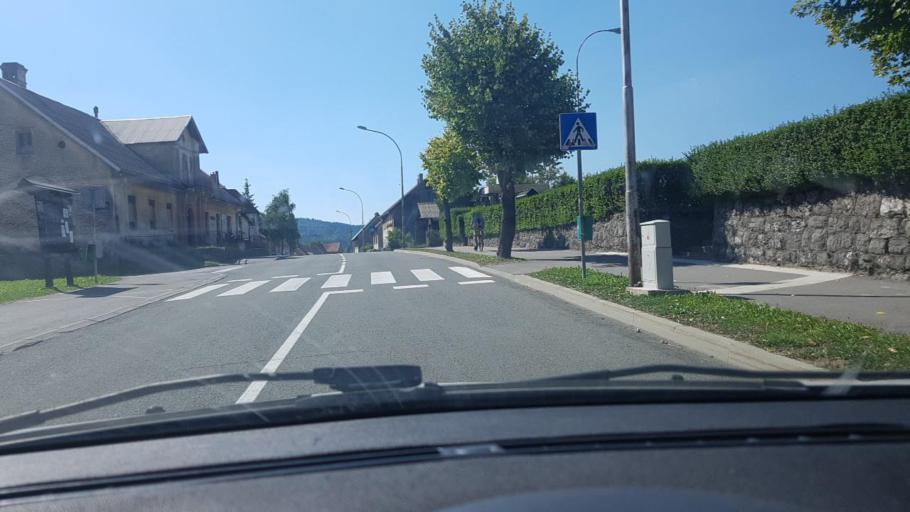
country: SI
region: Kostel
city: Kostel
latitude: 45.3735
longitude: 14.9370
